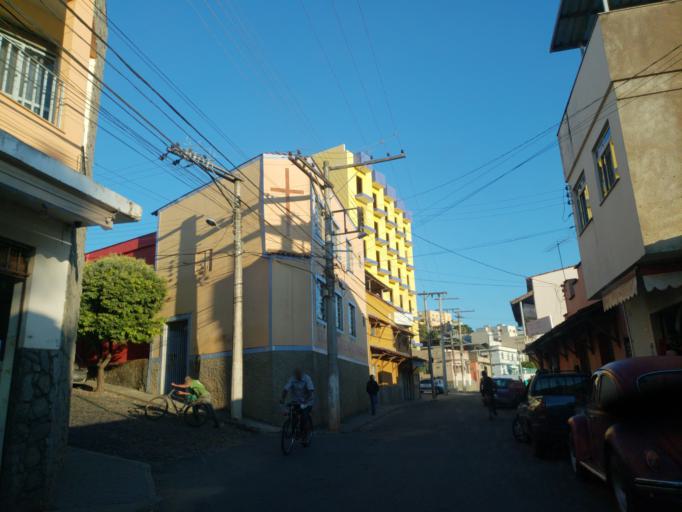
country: BR
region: Minas Gerais
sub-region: Sao Joao Nepomuceno
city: Sao Joao Nepomuceno
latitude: -21.5279
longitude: -43.0146
